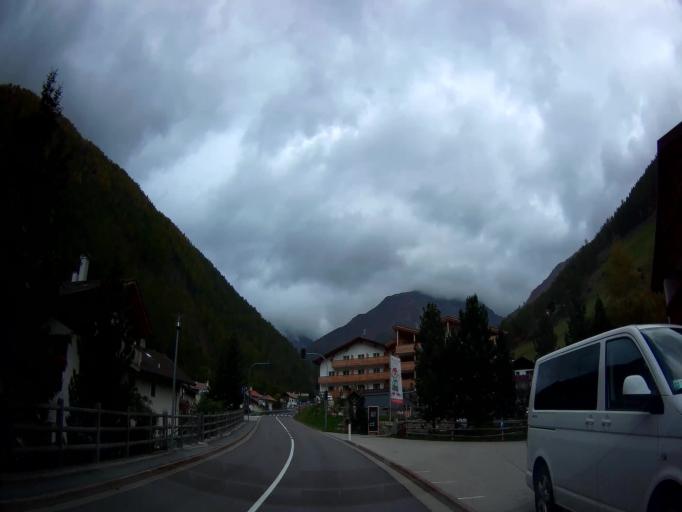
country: IT
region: Trentino-Alto Adige
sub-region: Bolzano
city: Senales
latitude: 46.7253
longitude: 10.8584
